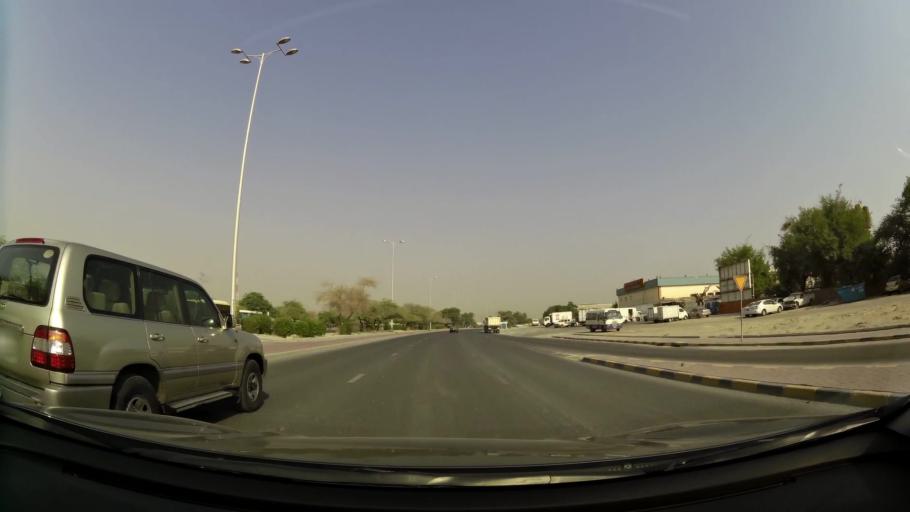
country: KW
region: Al Asimah
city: Ar Rabiyah
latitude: 29.2843
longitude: 47.8331
